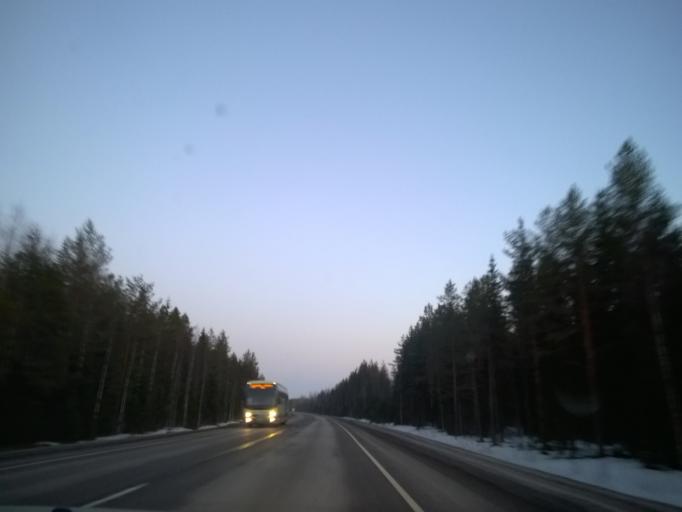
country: FI
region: Northern Ostrobothnia
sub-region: Nivala-Haapajaervi
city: Pyhaesalmi
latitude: 63.7882
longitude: 25.9236
